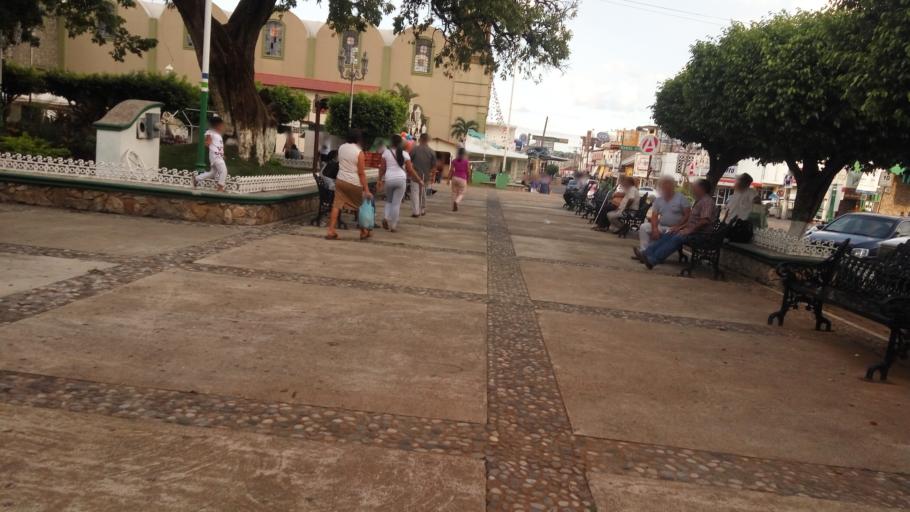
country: MX
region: Tabasco
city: Teapa
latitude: 17.5480
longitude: -92.9534
